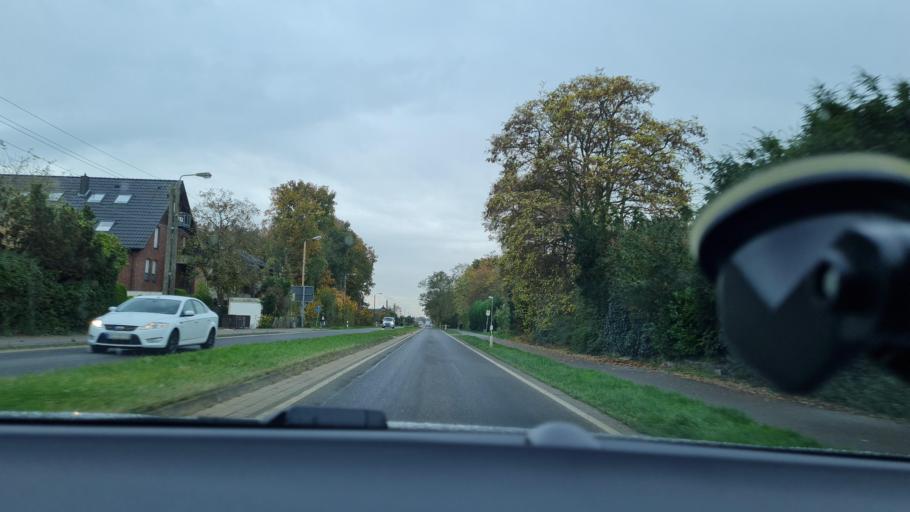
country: DE
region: North Rhine-Westphalia
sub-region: Regierungsbezirk Dusseldorf
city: Voerde
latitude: 51.6195
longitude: 6.6473
